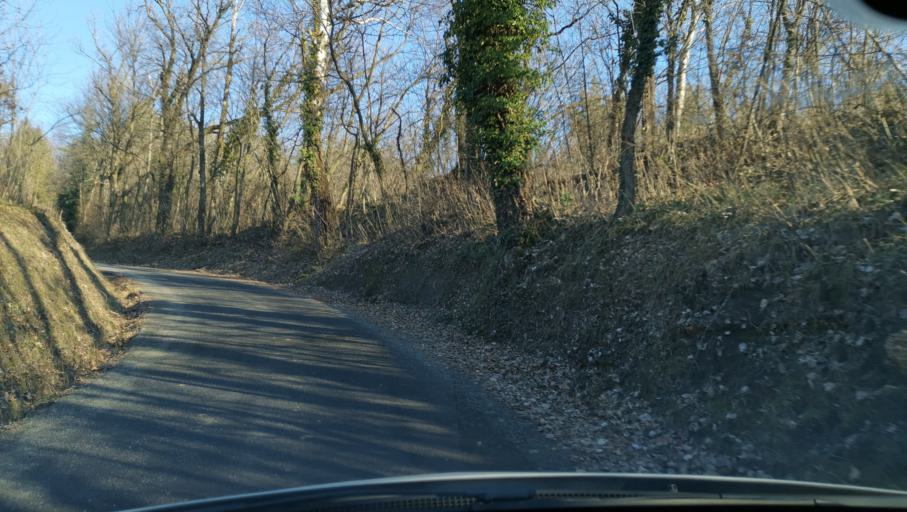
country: IT
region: Piedmont
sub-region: Provincia di Torino
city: San Raffaele Cimena
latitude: 45.1397
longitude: 7.8692
